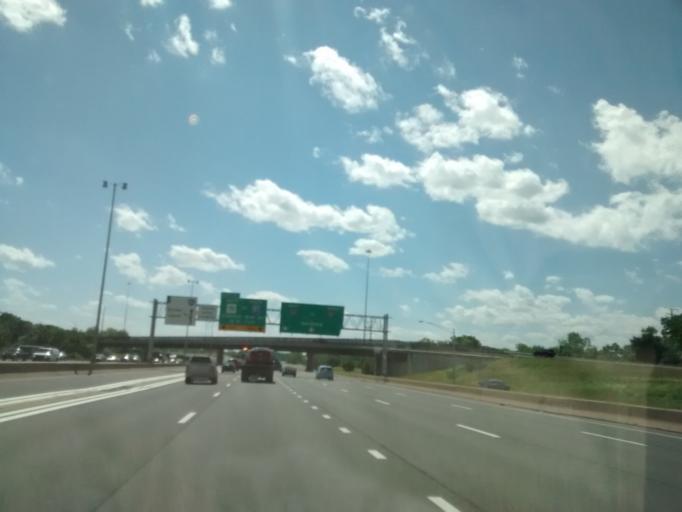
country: US
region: Connecticut
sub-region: Hartford County
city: East Hartford
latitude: 41.7663
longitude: -72.6235
